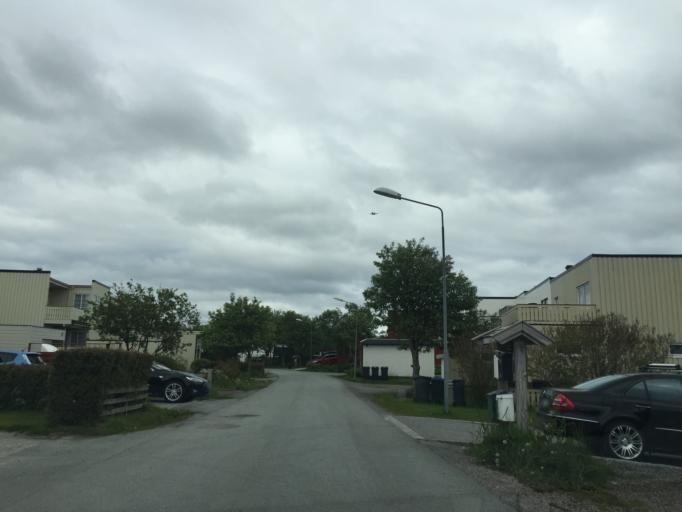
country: NO
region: Nordland
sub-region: Bodo
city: Lopsmarka
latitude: 67.2751
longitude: 14.5023
